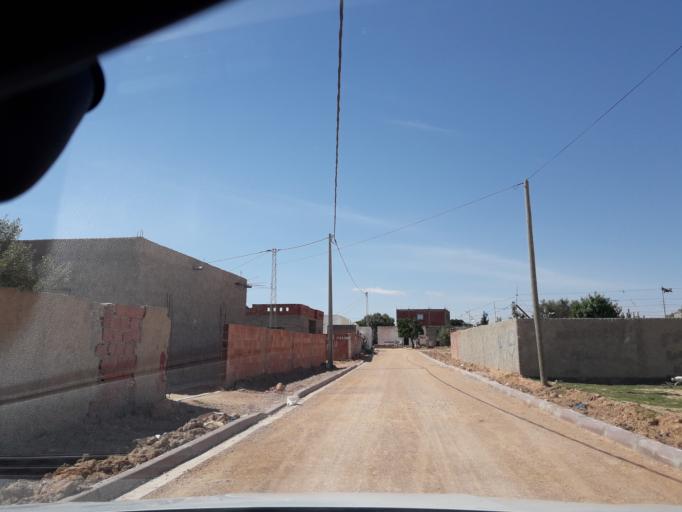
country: TN
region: Safaqis
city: Sfax
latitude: 34.7461
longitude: 10.5141
